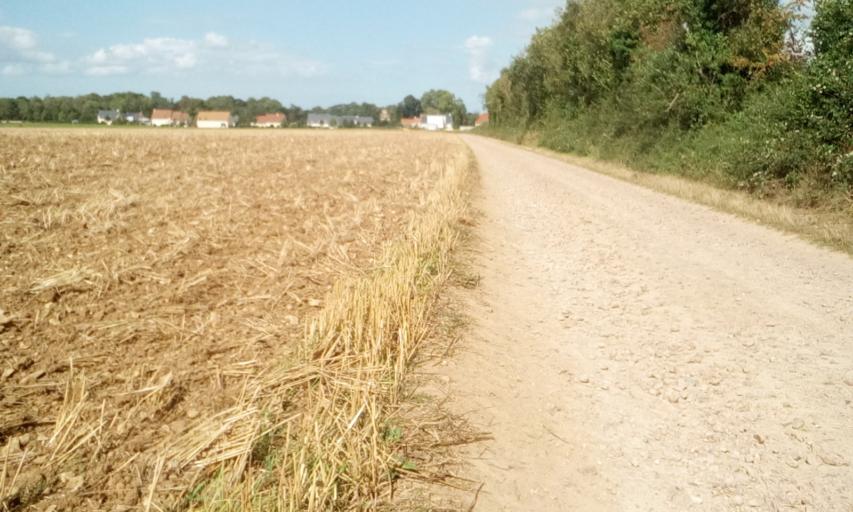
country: FR
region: Lower Normandy
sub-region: Departement du Calvados
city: Bellengreville
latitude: 49.1066
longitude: -0.2258
